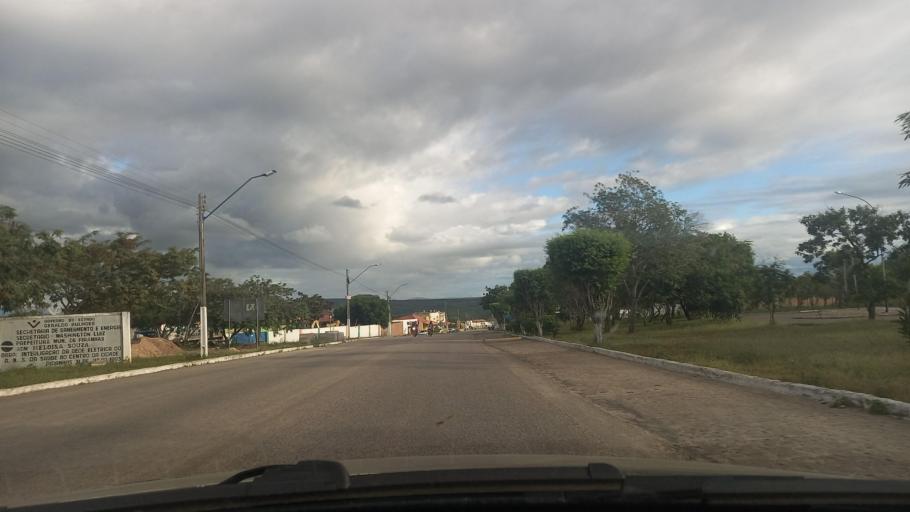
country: BR
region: Sergipe
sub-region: Caninde De Sao Francisco
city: Caninde de Sao Francisco
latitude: -9.6114
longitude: -37.7618
